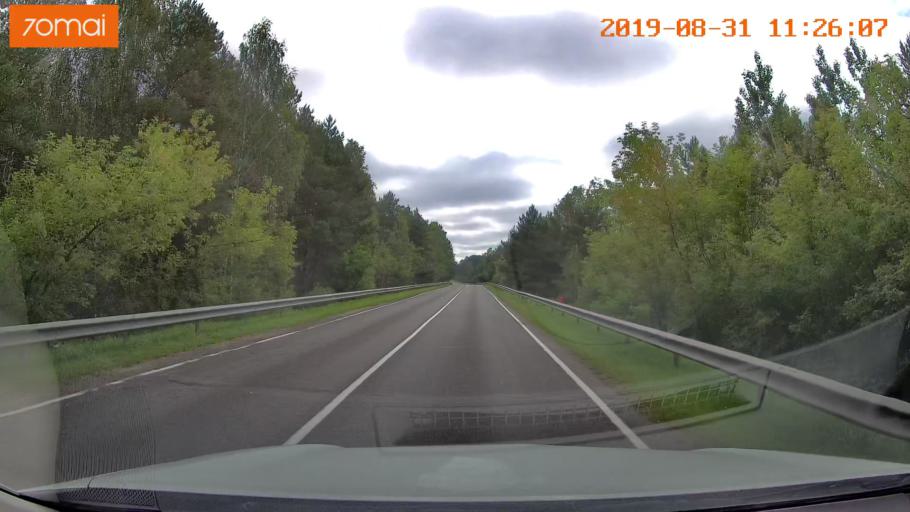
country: BY
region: Mogilev
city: Chavusy
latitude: 53.7651
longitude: 31.0627
